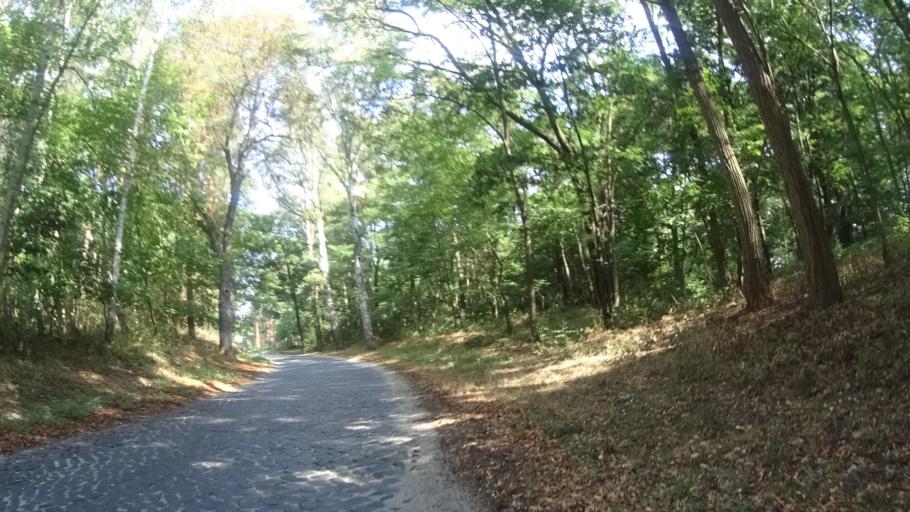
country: PL
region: Lubusz
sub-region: Powiat zarski
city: Leknica
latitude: 51.5076
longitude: 14.8375
